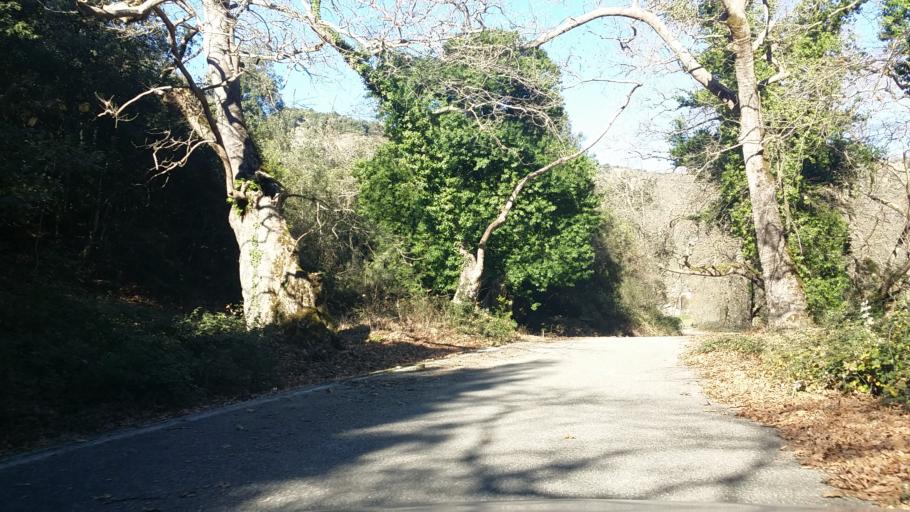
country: GR
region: West Greece
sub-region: Nomos Aitolias kai Akarnanias
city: Krikellos
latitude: 39.0115
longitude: 21.2385
